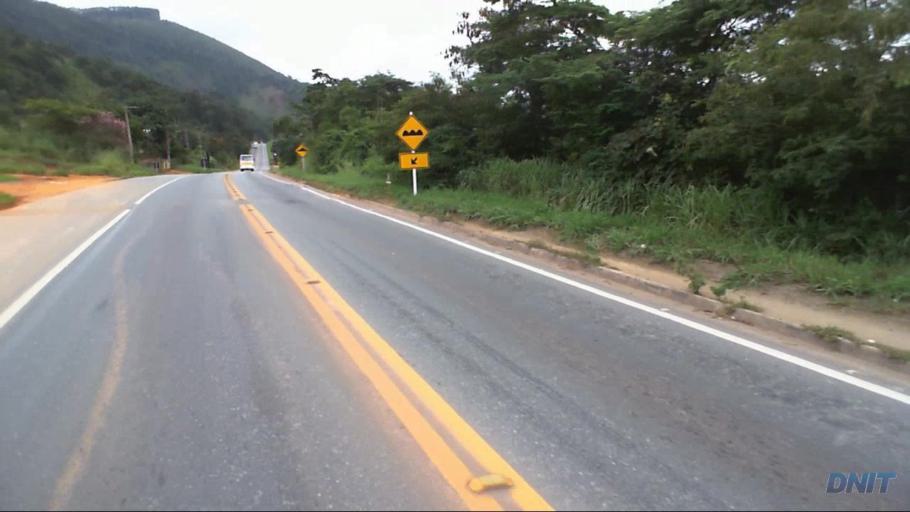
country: BR
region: Minas Gerais
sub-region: Nova Era
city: Nova Era
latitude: -19.7406
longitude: -43.0195
